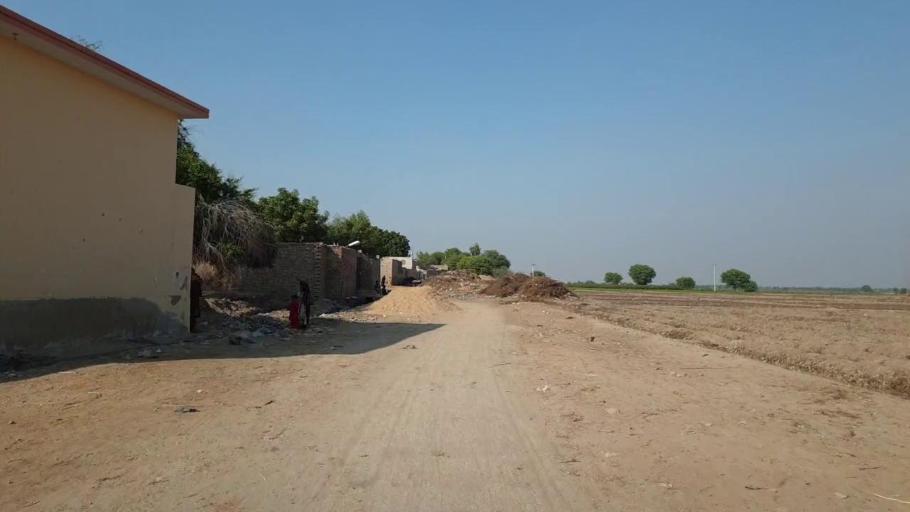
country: PK
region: Sindh
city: Sehwan
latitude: 26.4485
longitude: 67.8176
